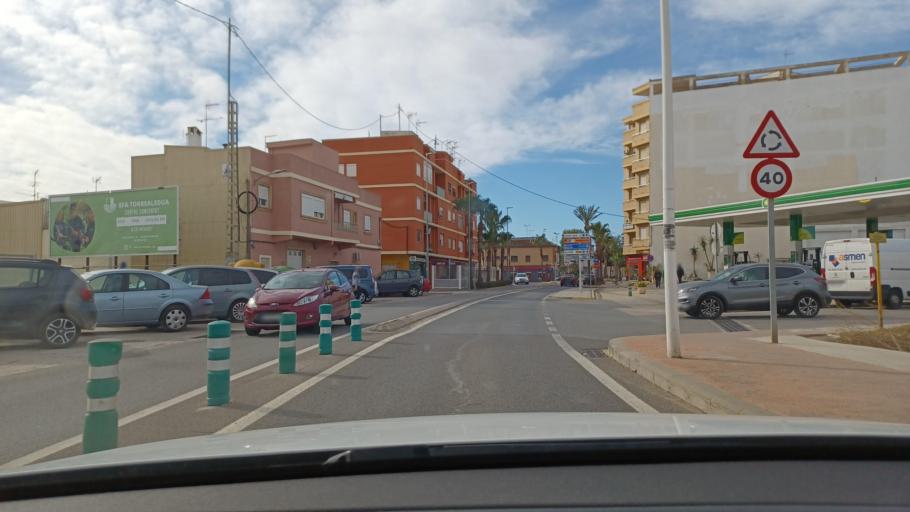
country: ES
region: Valencia
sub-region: Provincia de Valencia
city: Almussafes
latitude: 39.2891
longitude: -0.4201
